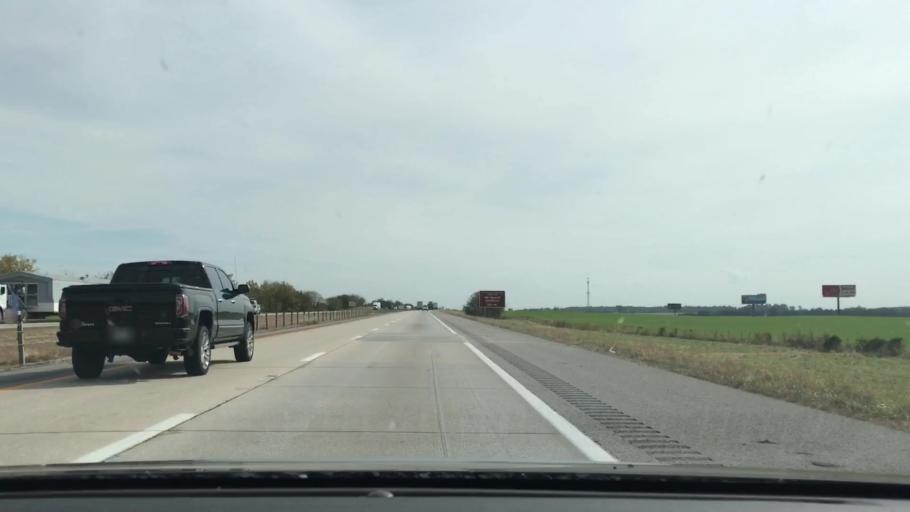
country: US
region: Kentucky
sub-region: Christian County
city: Oak Grove
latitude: 36.6920
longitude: -87.4274
